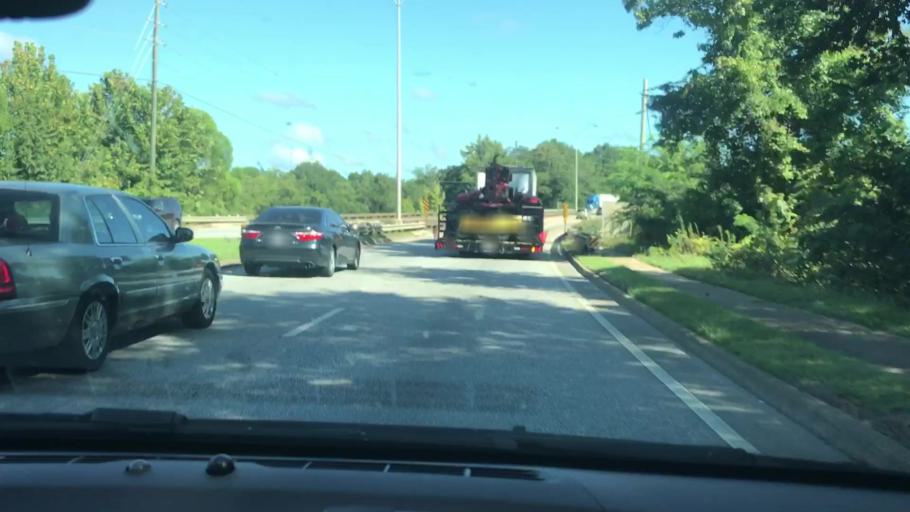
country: US
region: Alabama
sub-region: Barbour County
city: Eufaula
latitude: 31.9061
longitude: -85.1491
